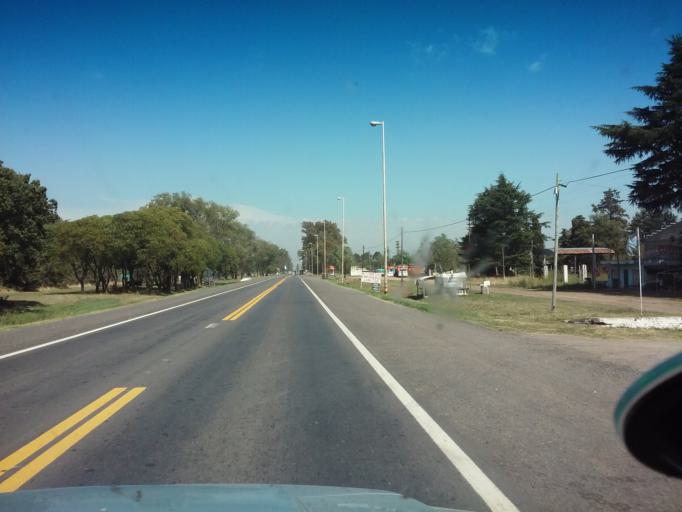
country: AR
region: Buenos Aires
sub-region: Partido de Nueve de Julio
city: Nueve de Julio
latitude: -35.4766
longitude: -60.8661
